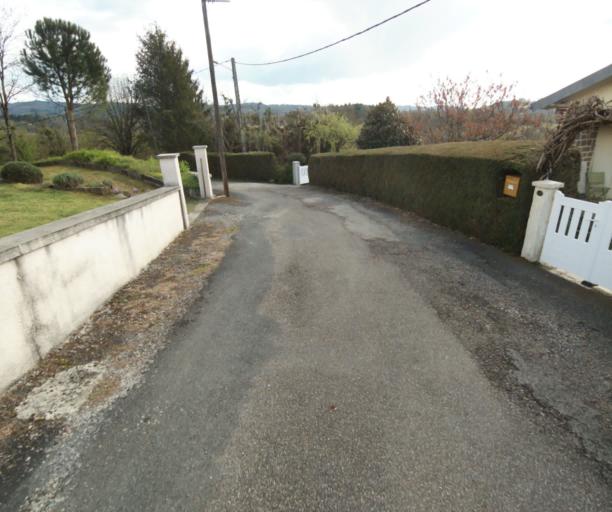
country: FR
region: Limousin
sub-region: Departement de la Correze
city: Tulle
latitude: 45.2511
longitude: 1.7447
